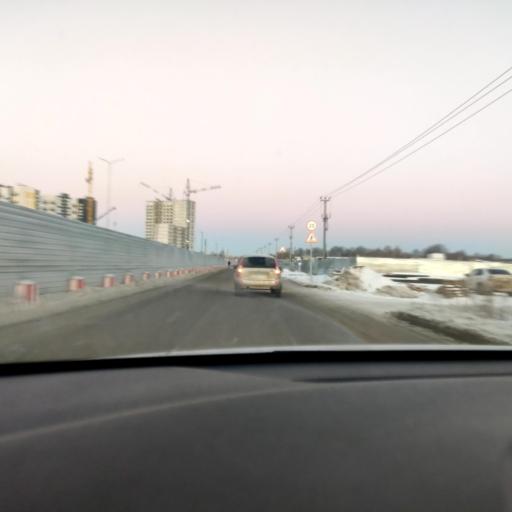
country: RU
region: Tatarstan
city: Osinovo
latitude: 55.8579
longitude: 48.9106
